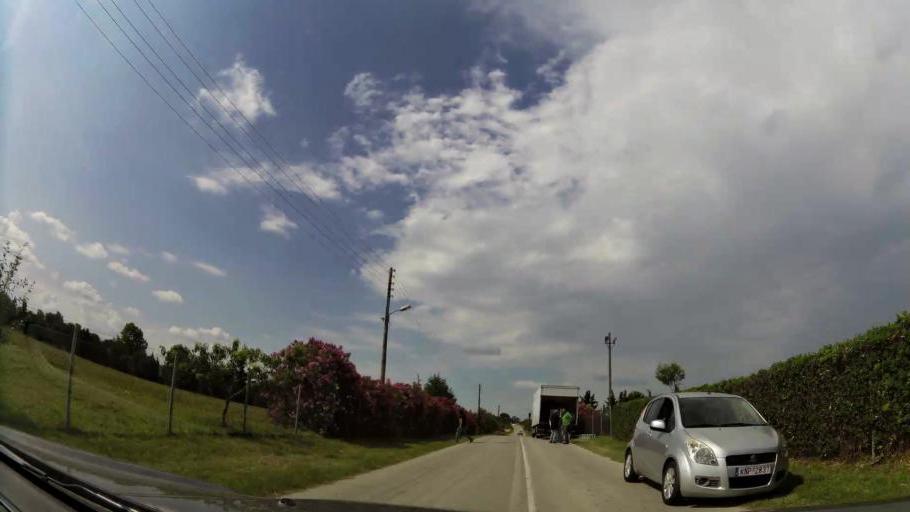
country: GR
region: Central Macedonia
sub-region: Nomos Pierias
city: Makrygialos
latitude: 40.3976
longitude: 22.6167
